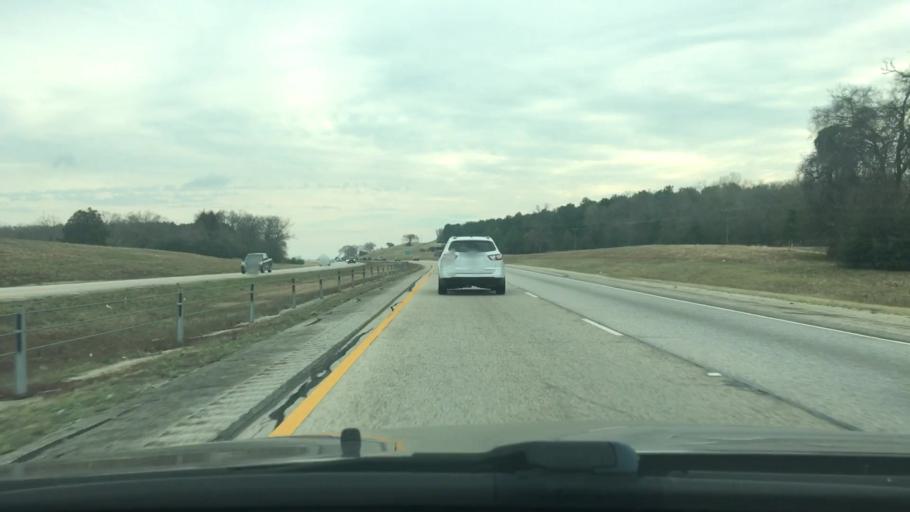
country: US
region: Texas
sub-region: Leon County
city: Centerville
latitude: 31.2961
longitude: -95.9987
